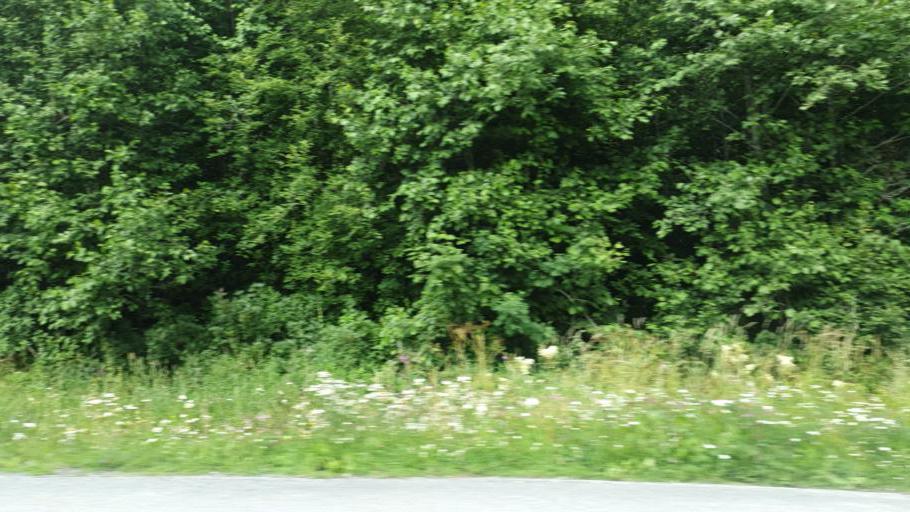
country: NO
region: Oppland
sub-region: Sel
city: Otta
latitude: 61.8424
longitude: 9.3898
